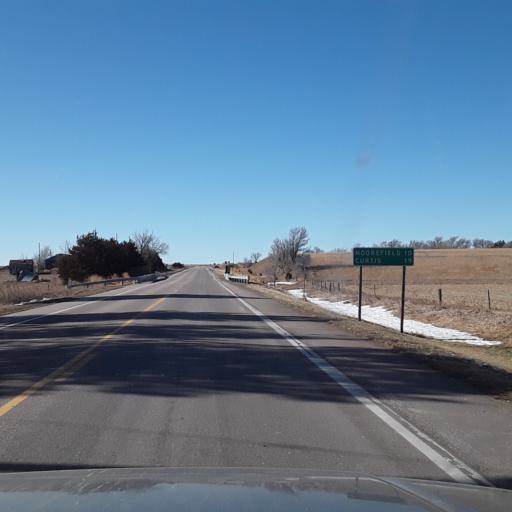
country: US
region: Nebraska
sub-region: Dawson County
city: Gothenburg
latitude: 40.7058
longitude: -100.2192
